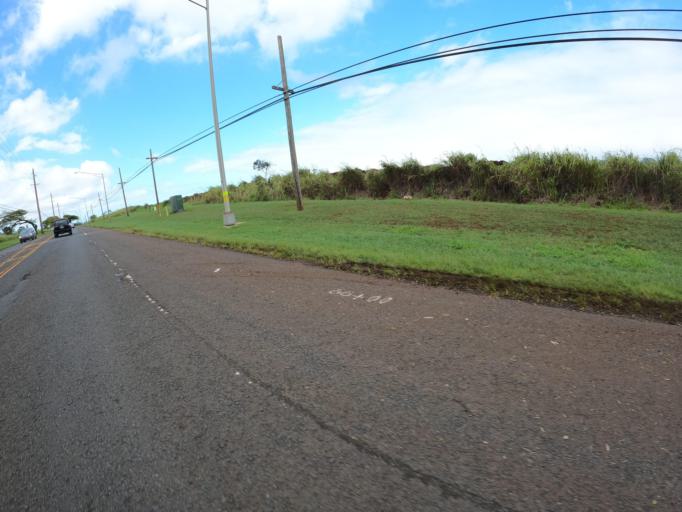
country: US
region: Hawaii
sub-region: Honolulu County
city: Wahiawa
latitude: 21.5064
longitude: -158.0343
